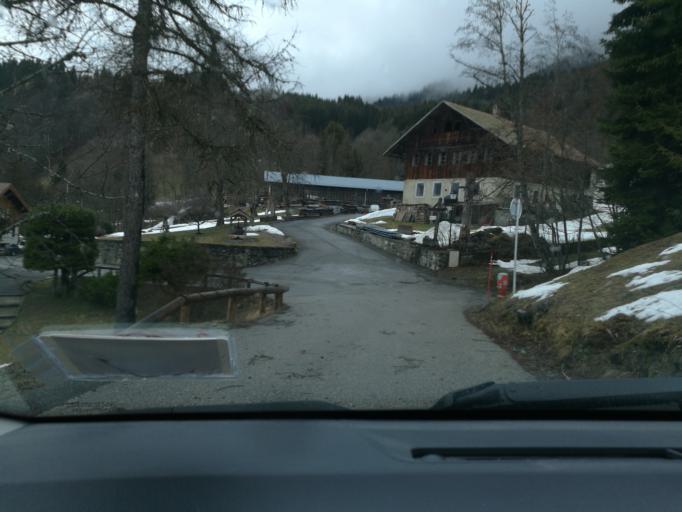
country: FR
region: Rhone-Alpes
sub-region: Departement de la Haute-Savoie
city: Araches-la-Frasse
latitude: 46.0559
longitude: 6.6314
